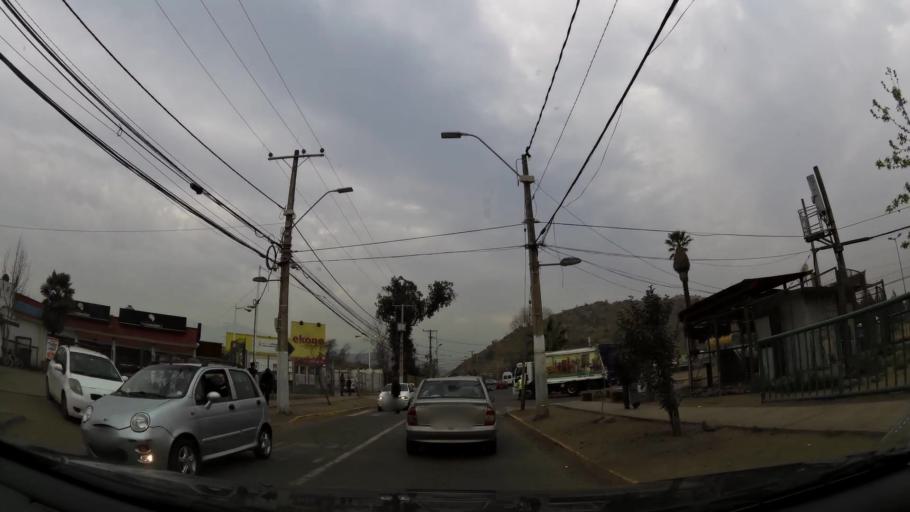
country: CL
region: Santiago Metropolitan
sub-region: Provincia de Chacabuco
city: Chicureo Abajo
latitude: -33.1920
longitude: -70.6644
